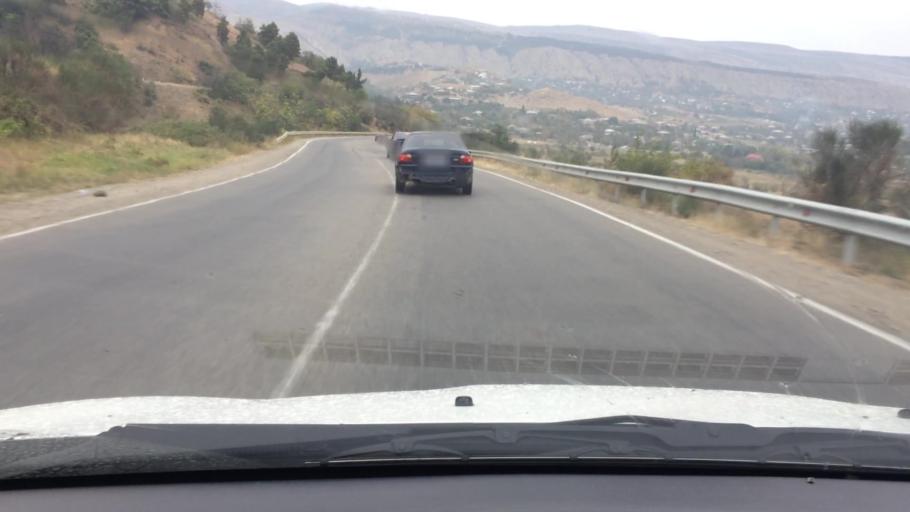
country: GE
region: T'bilisi
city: Tbilisi
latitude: 41.5942
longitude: 44.7804
